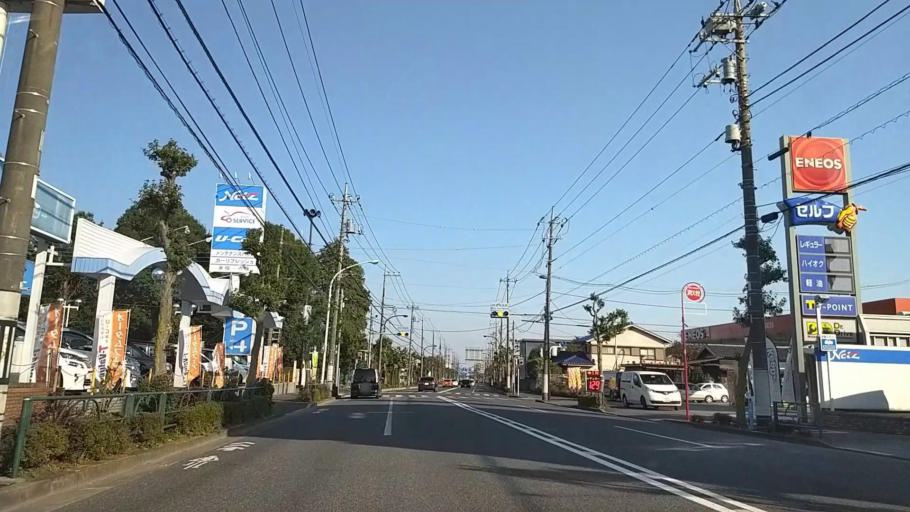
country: JP
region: Tokyo
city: Ome
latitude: 35.7881
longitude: 139.2950
